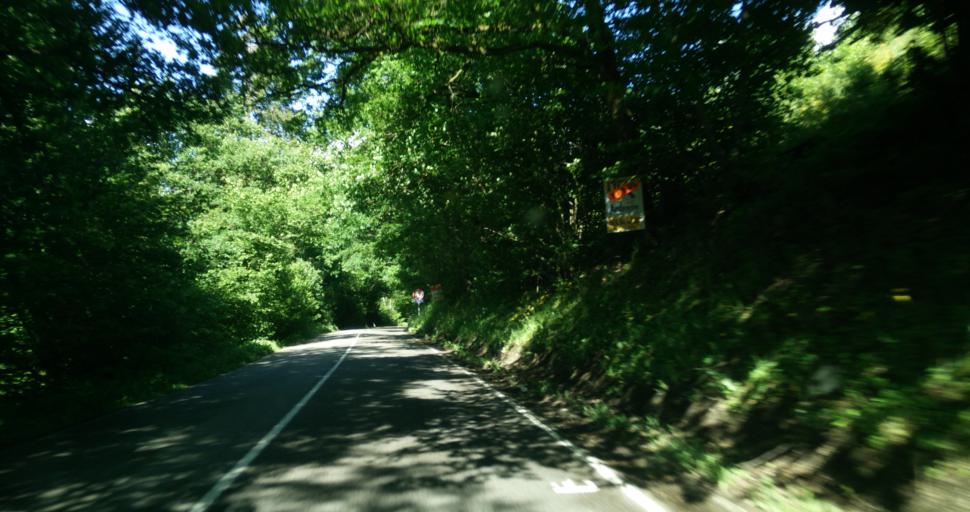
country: BE
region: Wallonia
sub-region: Province du Luxembourg
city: La Roche-en-Ardenne
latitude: 50.1858
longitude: 5.5276
